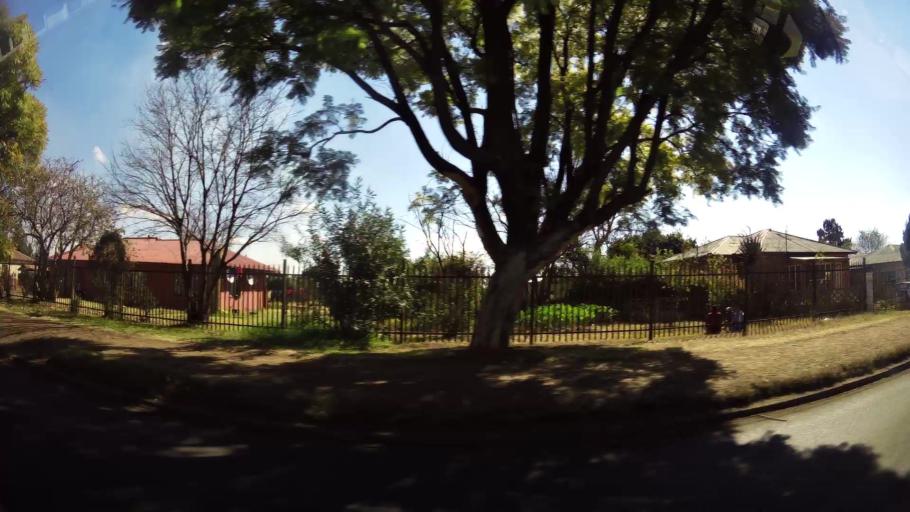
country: ZA
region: Mpumalanga
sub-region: Nkangala District Municipality
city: Witbank
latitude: -25.8688
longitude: 29.2147
